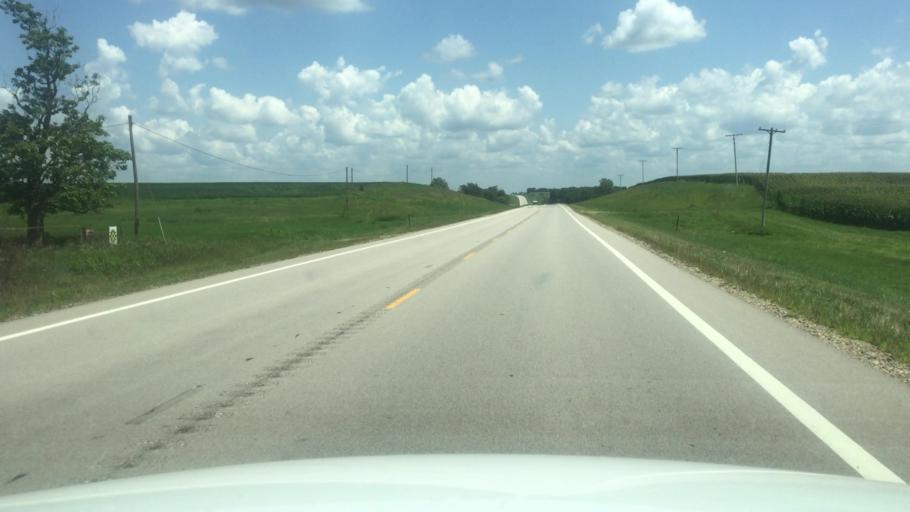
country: US
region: Kansas
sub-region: Brown County
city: Horton
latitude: 39.6674
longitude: -95.4846
